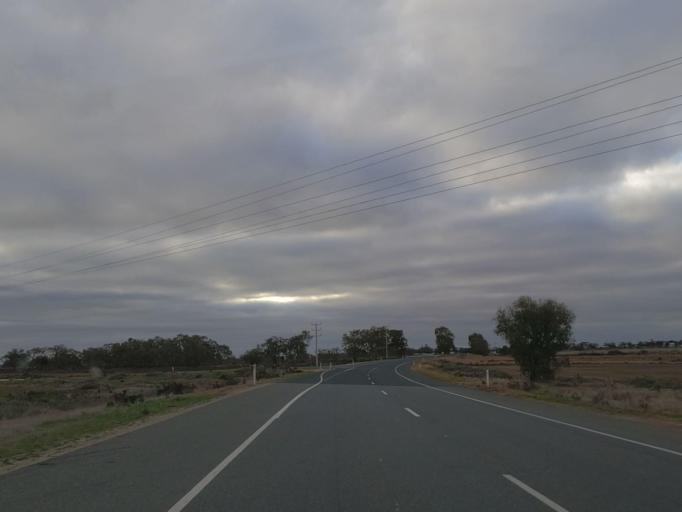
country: AU
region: Victoria
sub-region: Swan Hill
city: Swan Hill
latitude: -35.6219
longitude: 143.8040
